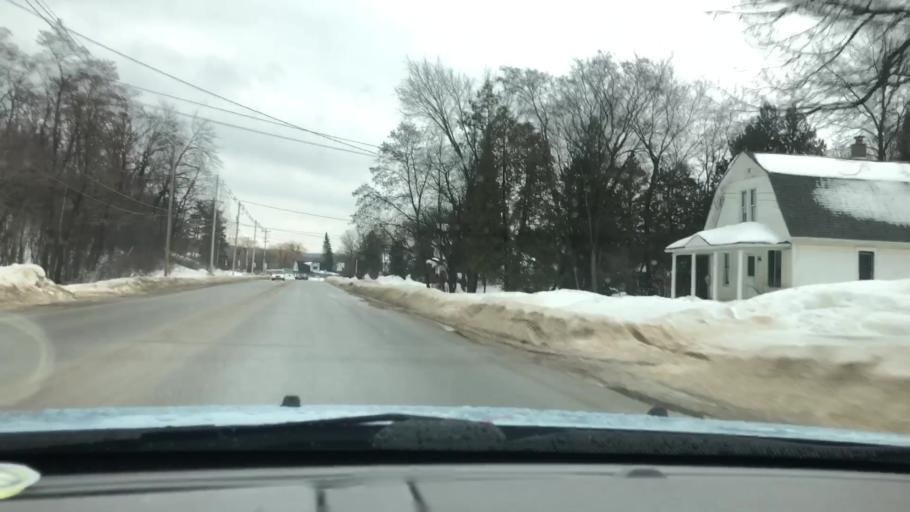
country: US
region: Michigan
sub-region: Charlevoix County
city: East Jordan
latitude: 45.1531
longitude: -85.1216
